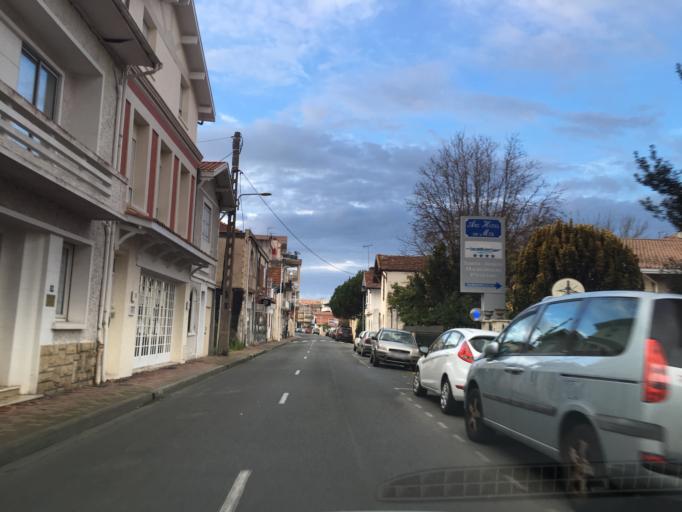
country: FR
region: Aquitaine
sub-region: Departement de la Gironde
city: Arcachon
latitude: 44.6611
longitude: -1.1559
